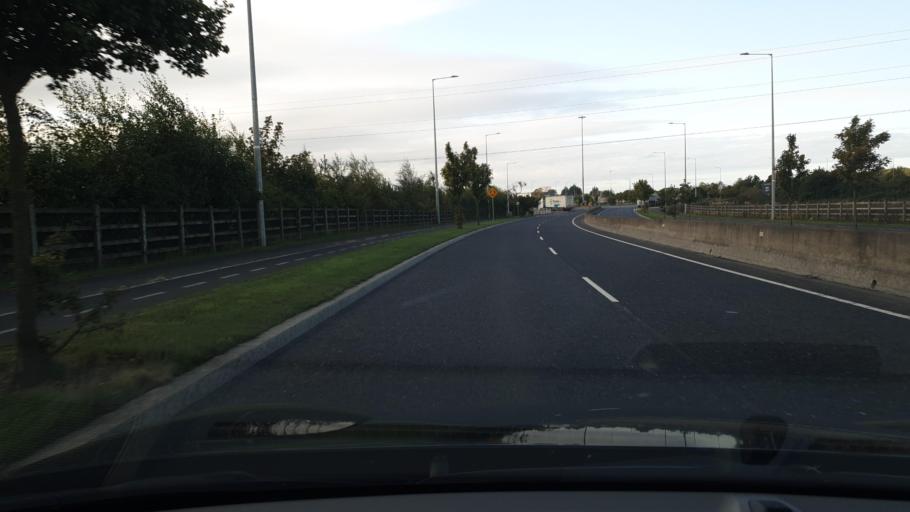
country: IE
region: Leinster
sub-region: Fingal County
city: Blanchardstown
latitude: 53.4303
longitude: -6.3489
